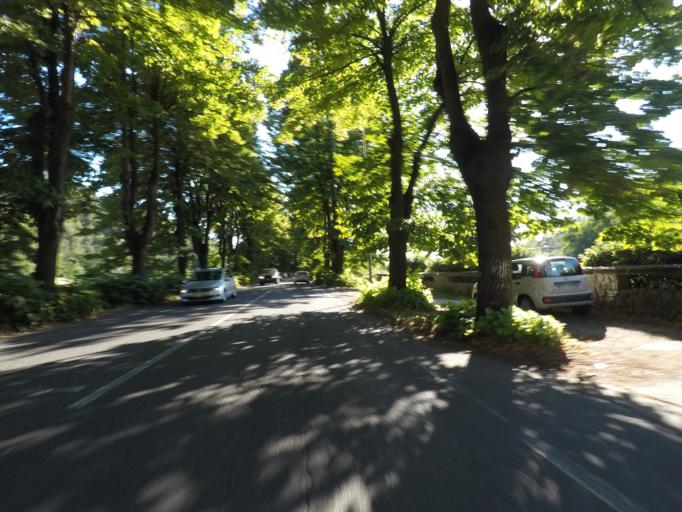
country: IT
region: Tuscany
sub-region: Provincia di Lucca
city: Piano di Mommio
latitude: 43.9336
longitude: 10.2806
